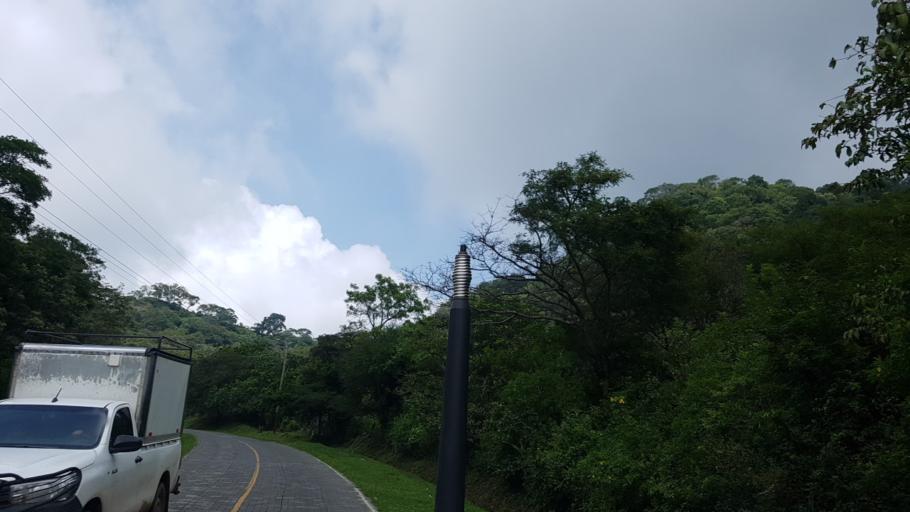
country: NI
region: Leon
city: Santa Rosa del Penon
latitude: 12.9349
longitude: -86.3404
